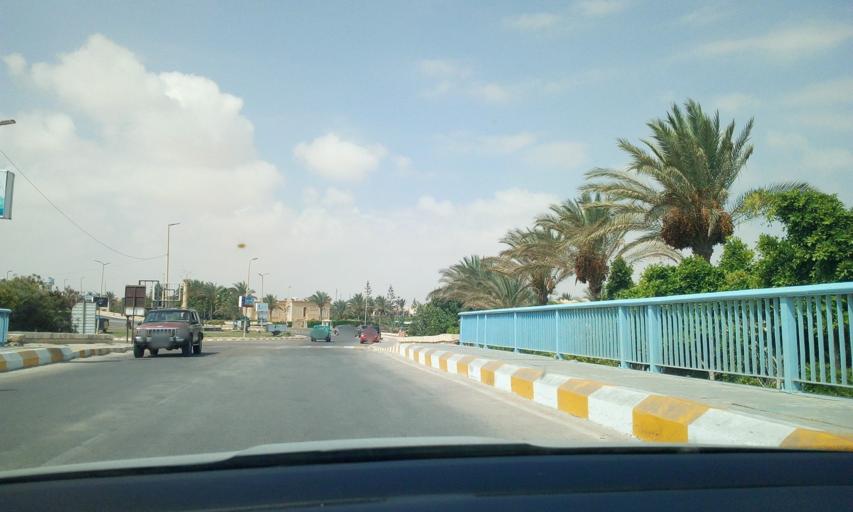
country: EG
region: Muhafazat Matruh
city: Al `Alamayn
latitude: 30.8435
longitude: 28.9739
